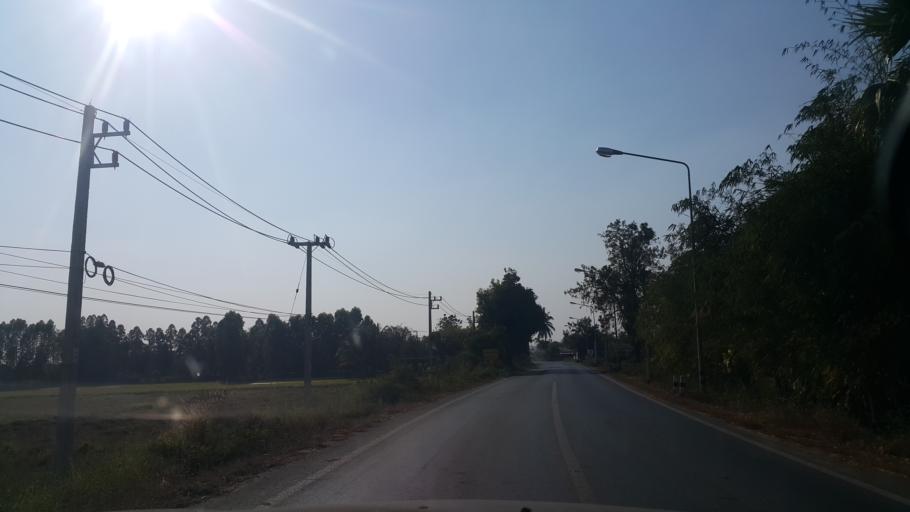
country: TH
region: Nakhon Ratchasima
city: Phimai
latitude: 15.1709
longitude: 102.4000
